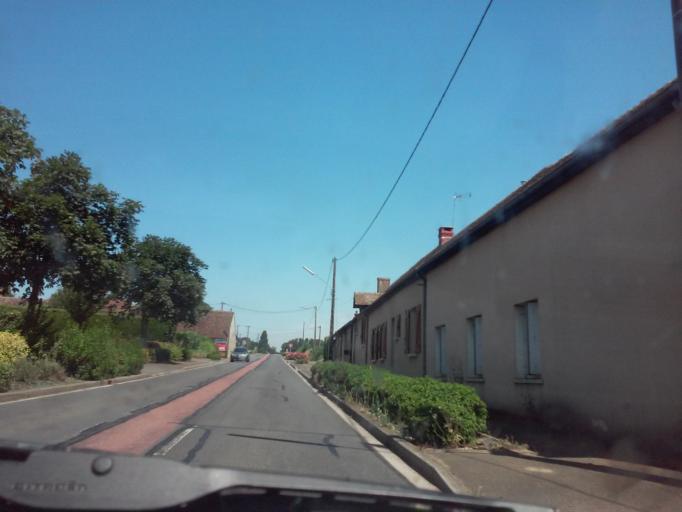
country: FR
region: Pays de la Loire
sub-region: Departement de la Sarthe
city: Beaufay
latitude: 48.1106
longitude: 0.3388
